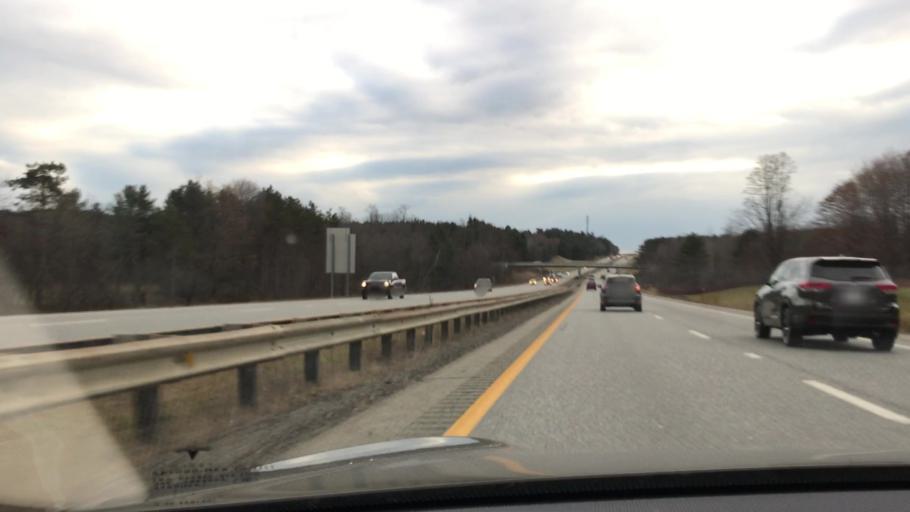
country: US
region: Maine
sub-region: Kennebec County
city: Hallowell
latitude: 44.2801
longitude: -69.8065
